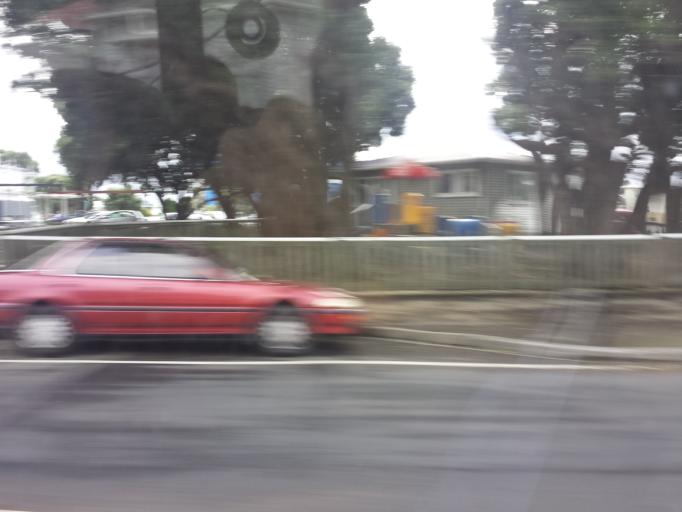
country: NZ
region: Wellington
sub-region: Wellington City
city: Wellington
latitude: -41.3169
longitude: 174.7948
